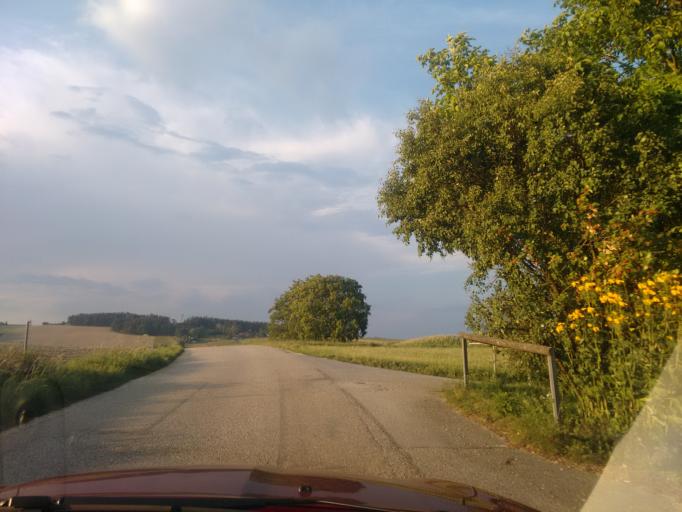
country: AT
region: Upper Austria
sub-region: Politischer Bezirk Grieskirchen
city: Bad Schallerbach
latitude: 48.1903
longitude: 13.9001
